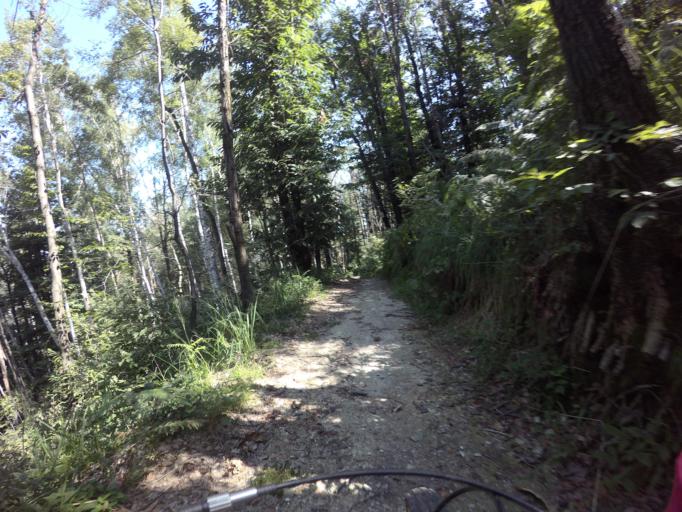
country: IT
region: Piedmont
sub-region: Provincia di Cuneo
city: Chiusa di Pesio
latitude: 44.2968
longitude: 7.6921
